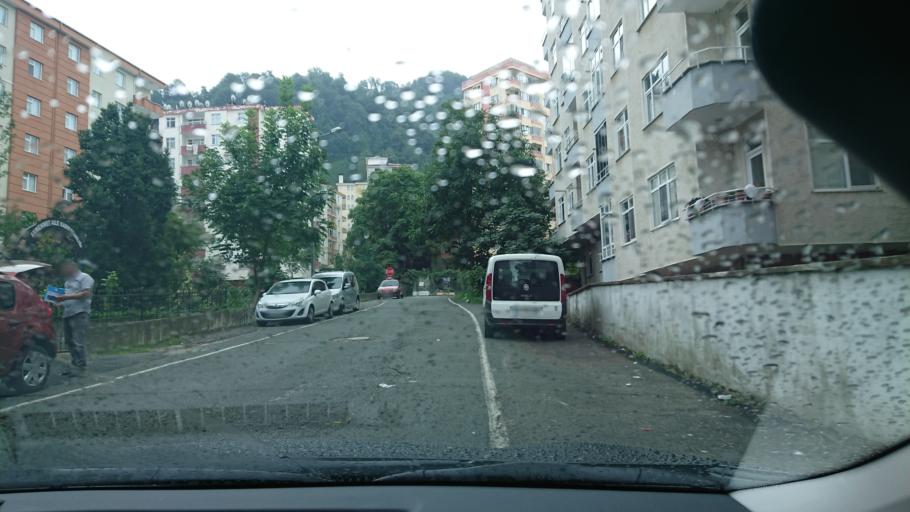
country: TR
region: Rize
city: Rize
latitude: 41.0258
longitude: 40.5466
